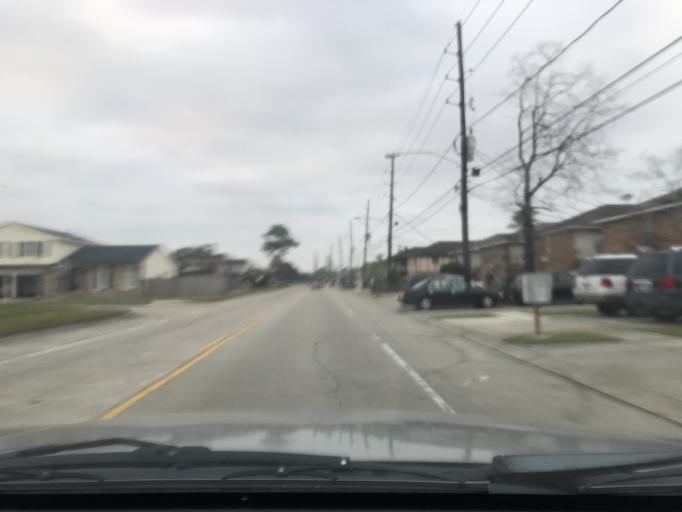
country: US
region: Louisiana
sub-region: Jefferson Parish
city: Woodmere
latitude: 29.8621
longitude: -90.0751
